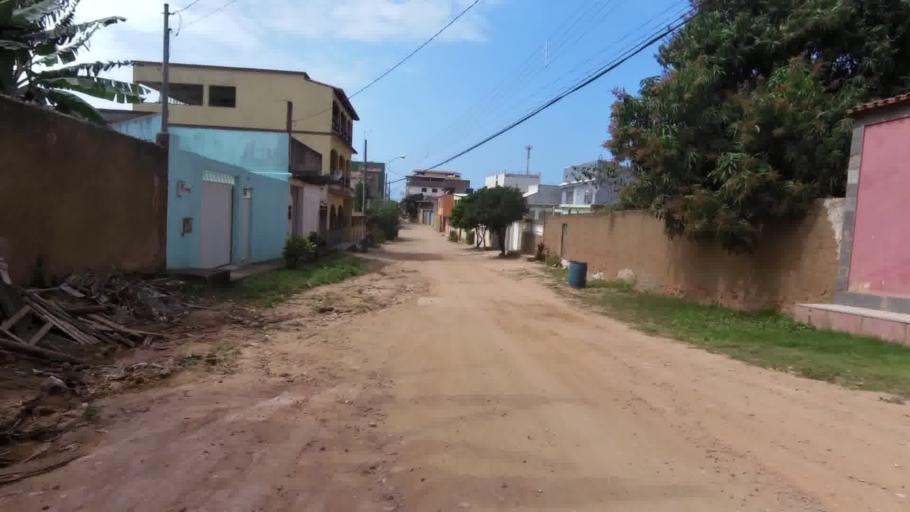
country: BR
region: Espirito Santo
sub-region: Itapemirim
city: Itapemirim
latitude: -21.0236
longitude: -40.8183
